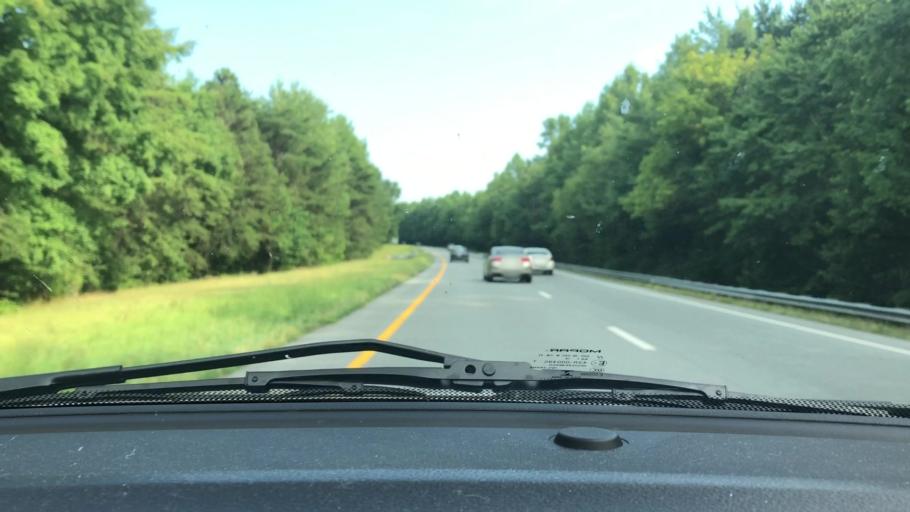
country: US
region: North Carolina
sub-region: Randolph County
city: Liberty
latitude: 35.8692
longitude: -79.6292
